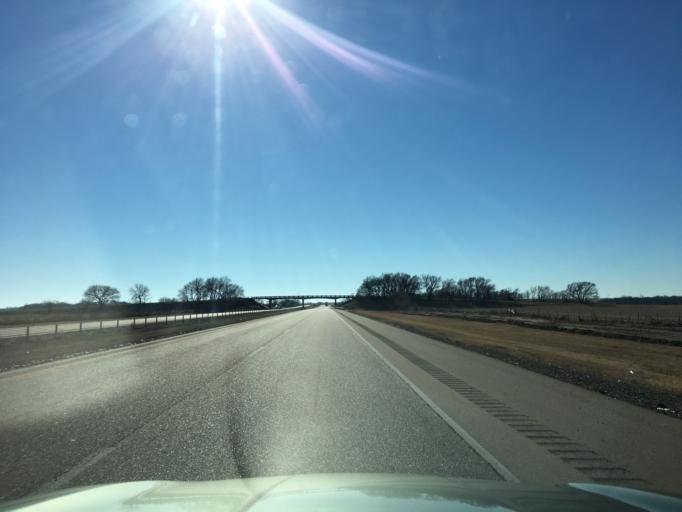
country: US
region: Oklahoma
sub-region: Kay County
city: Blackwell
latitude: 36.9156
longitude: -97.3516
